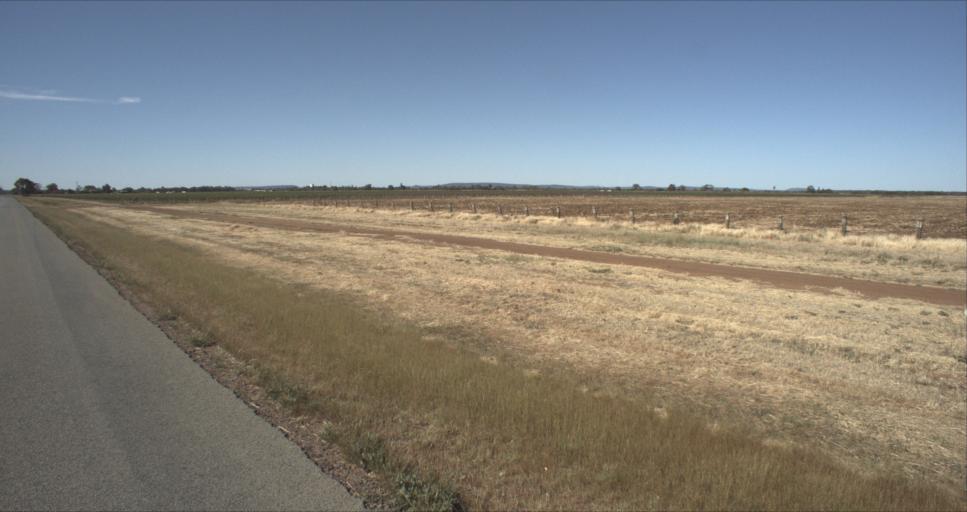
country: AU
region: New South Wales
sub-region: Leeton
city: Leeton
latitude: -34.5825
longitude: 146.3796
